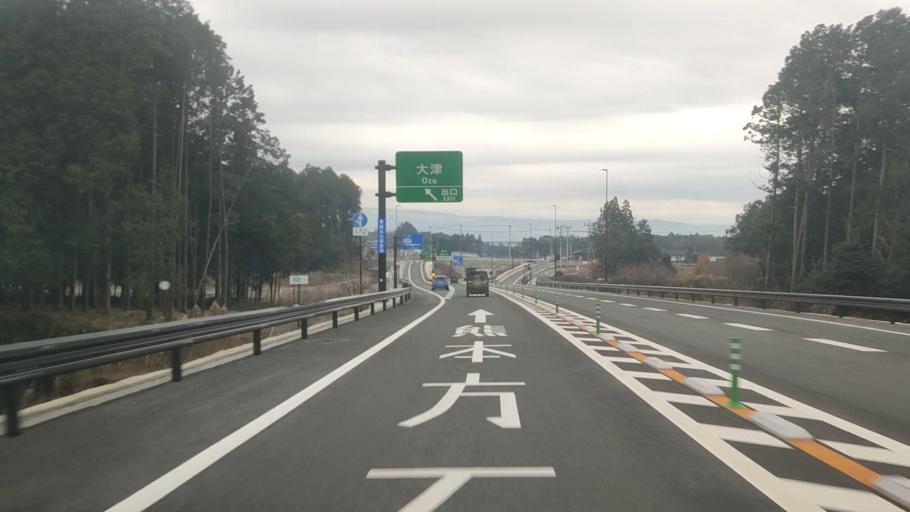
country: JP
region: Kumamoto
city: Ozu
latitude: 32.8930
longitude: 130.8961
